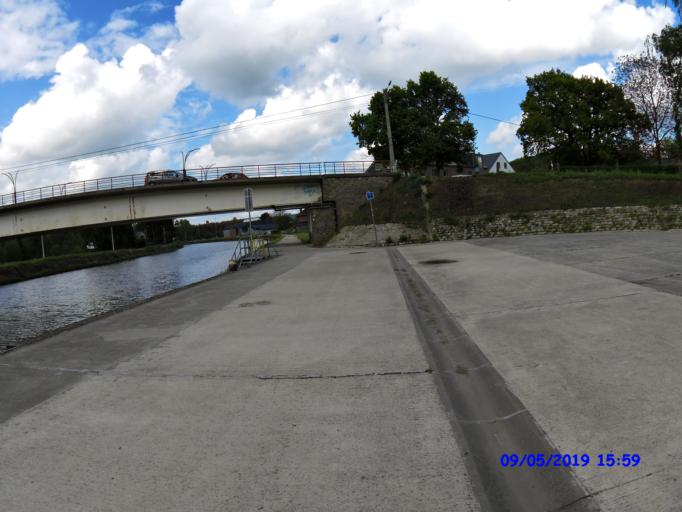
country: BE
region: Wallonia
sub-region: Province de Namur
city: Floreffe
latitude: 50.4345
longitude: 4.7566
